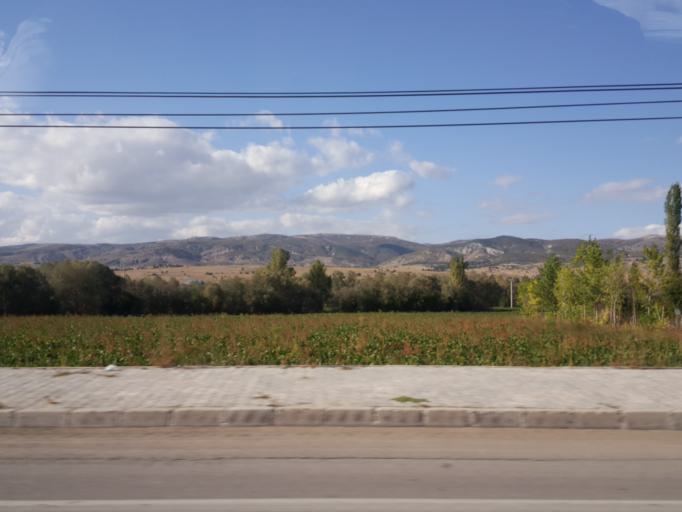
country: TR
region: Tokat
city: Yesilyurt
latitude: 40.0115
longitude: 36.2275
